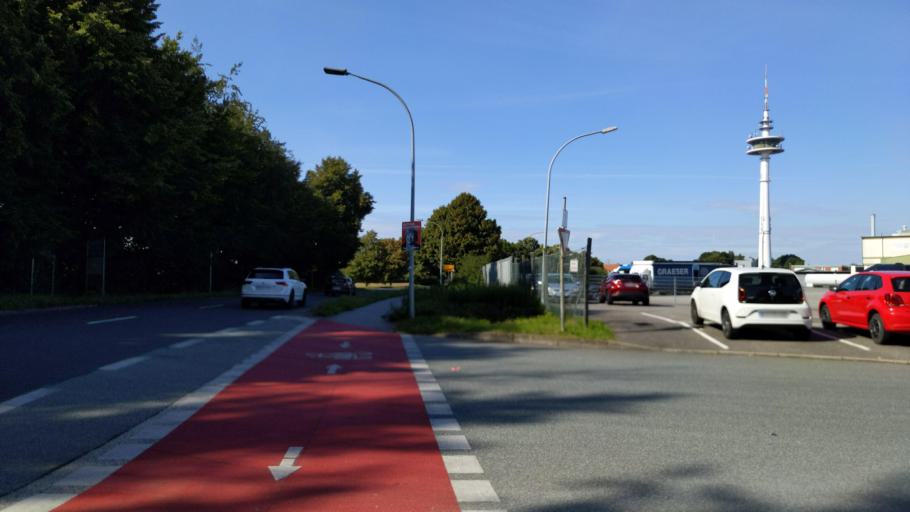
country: DE
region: Schleswig-Holstein
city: Stockelsdorf
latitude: 53.9019
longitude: 10.6429
